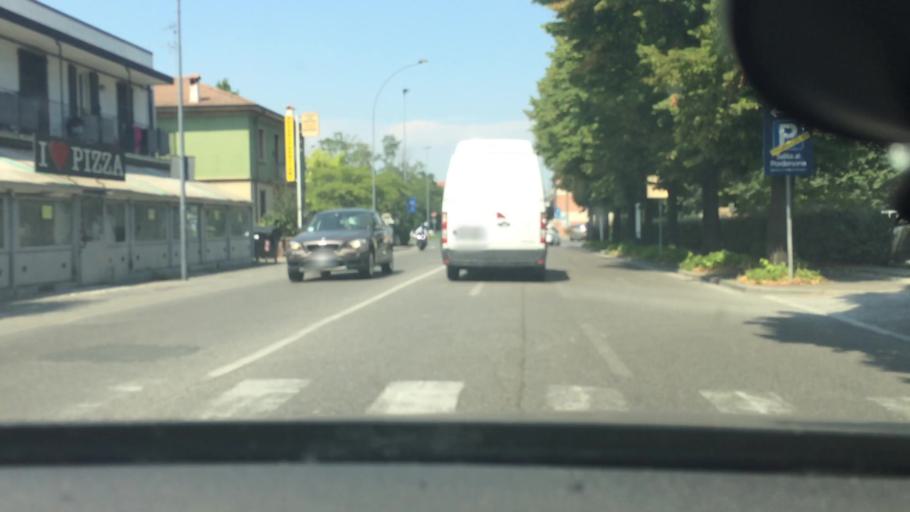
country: IT
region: Emilia-Romagna
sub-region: Provincia di Piacenza
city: Piacenza
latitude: 45.0561
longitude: 9.6777
